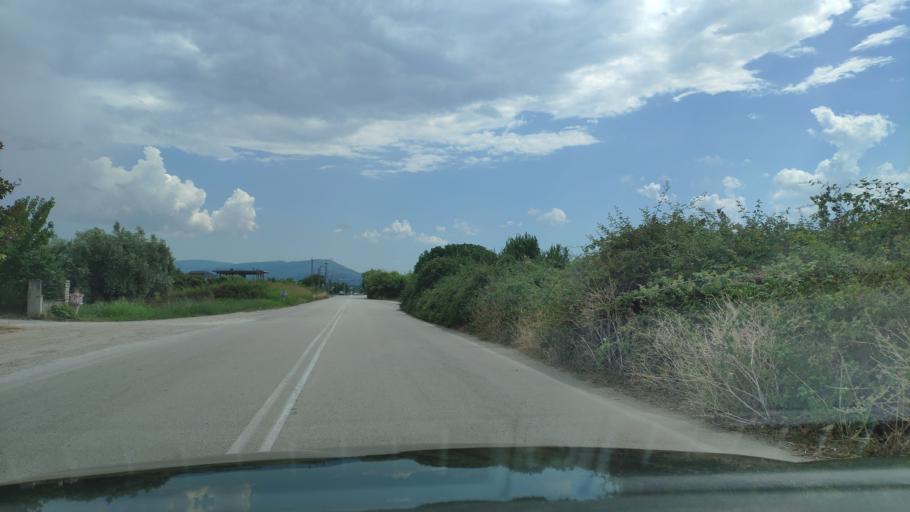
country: GR
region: West Greece
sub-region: Nomos Aitolias kai Akarnanias
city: Krikellos
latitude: 38.9525
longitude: 21.1759
